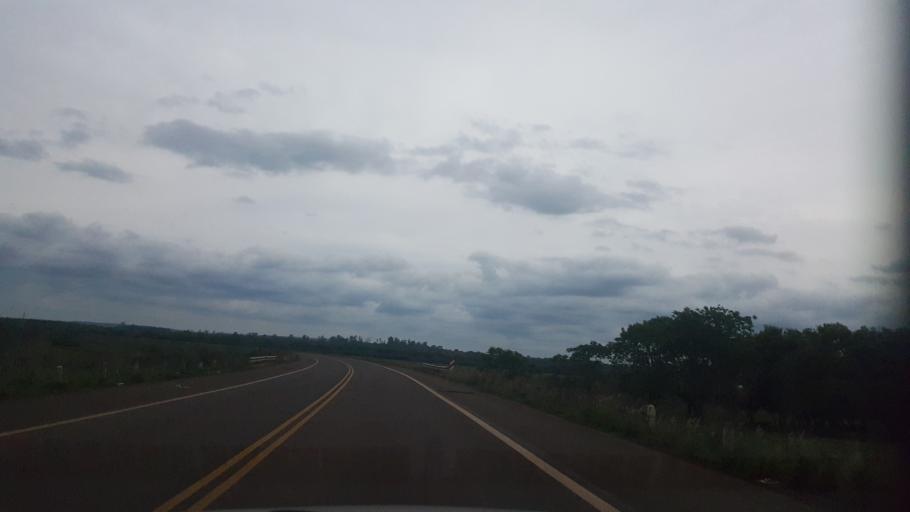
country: AR
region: Misiones
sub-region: Departamento de Candelaria
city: Candelaria
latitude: -27.4812
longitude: -55.7471
